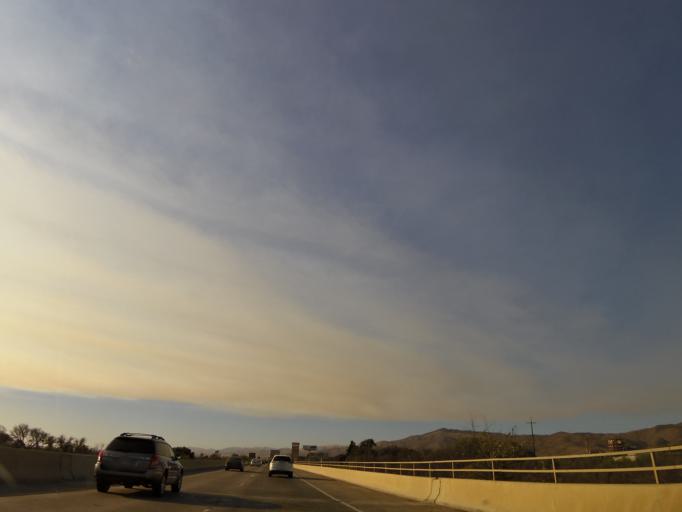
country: US
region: California
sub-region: Monterey County
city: Soledad
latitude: 36.4098
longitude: -121.3192
